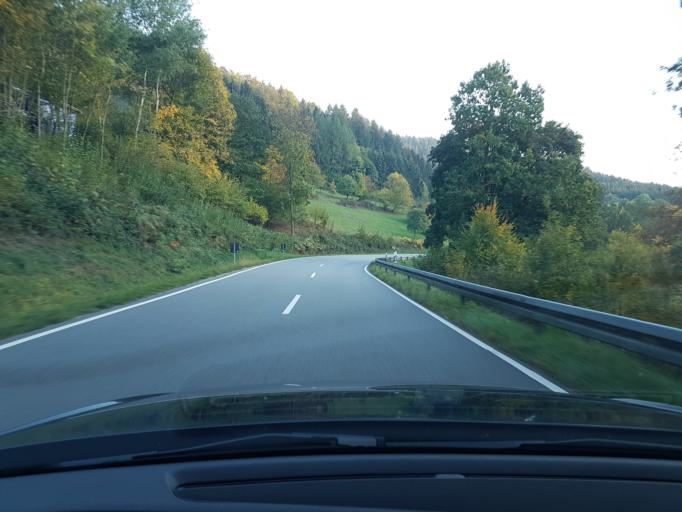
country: DE
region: Hesse
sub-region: Regierungsbezirk Darmstadt
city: Rothenberg
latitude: 49.5113
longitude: 8.9659
